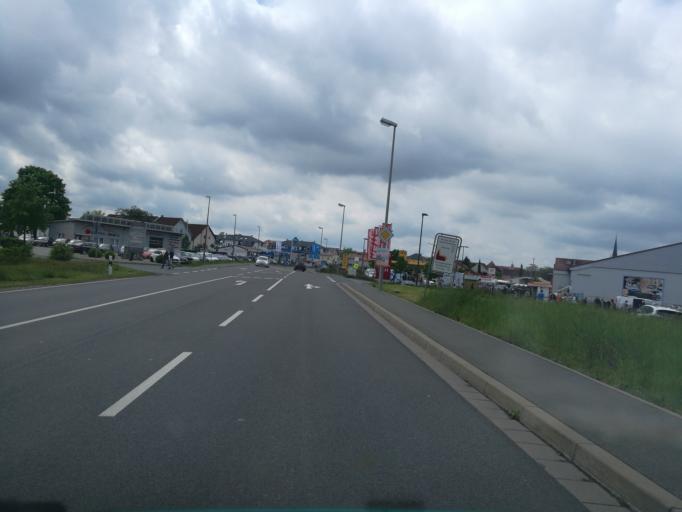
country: DE
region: Bavaria
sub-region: Upper Franconia
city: Bad Staffelstein
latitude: 50.1055
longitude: 11.0075
